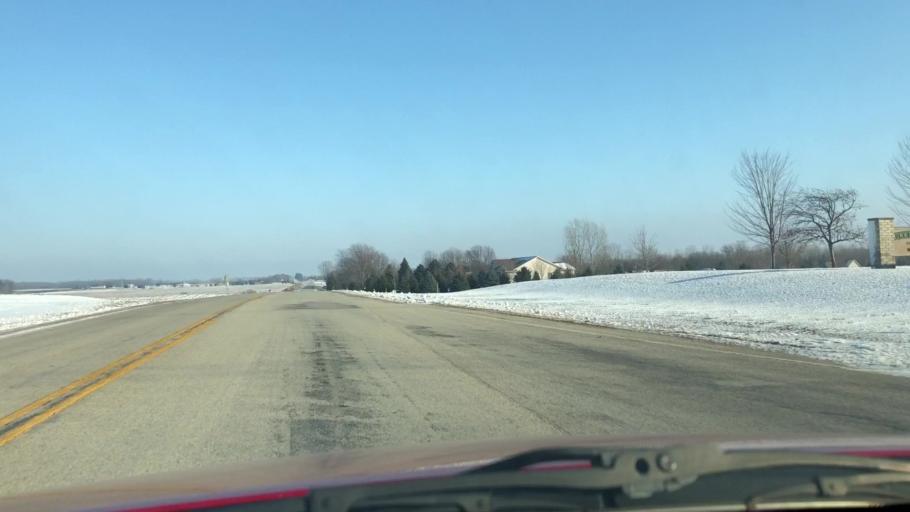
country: US
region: Wisconsin
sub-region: Outagamie County
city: Seymour
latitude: 44.4436
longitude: -88.3553
